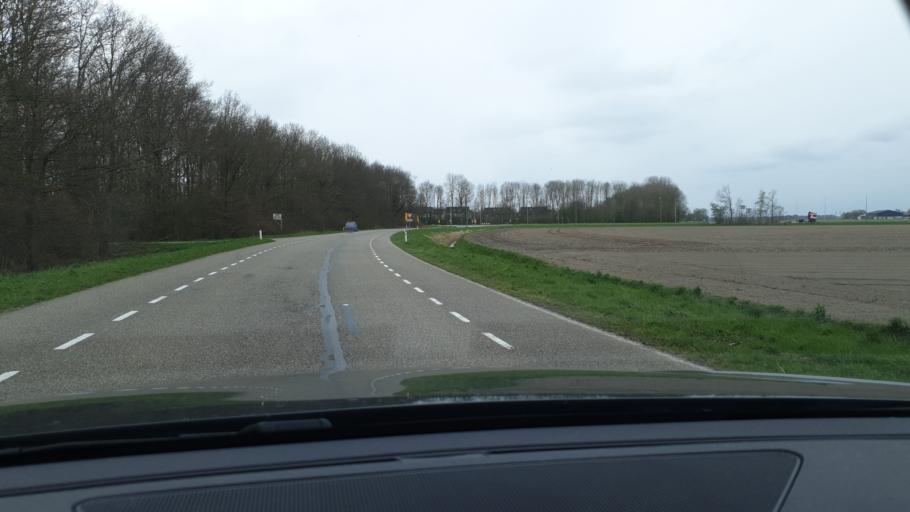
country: NL
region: Flevoland
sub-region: Gemeente Dronten
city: Dronten
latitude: 52.5759
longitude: 5.6478
